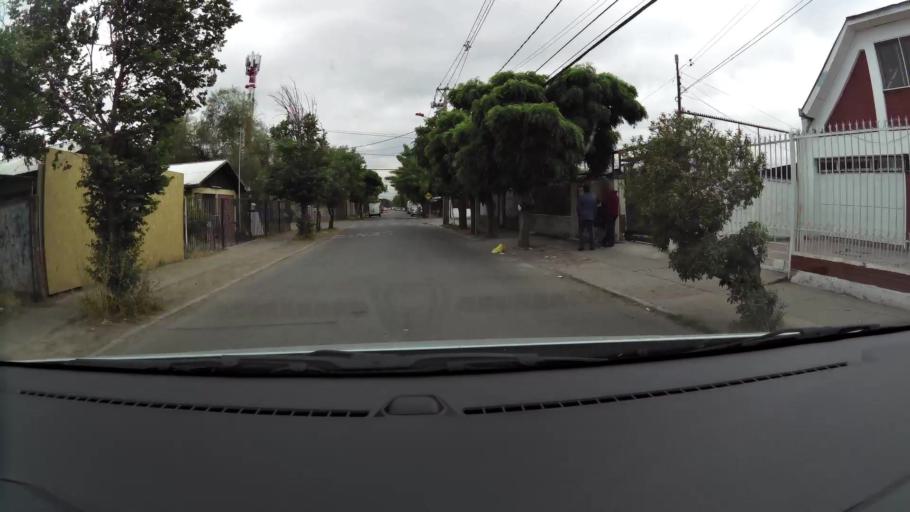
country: CL
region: Santiago Metropolitan
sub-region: Provincia de Santiago
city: Santiago
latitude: -33.5015
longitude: -70.6875
